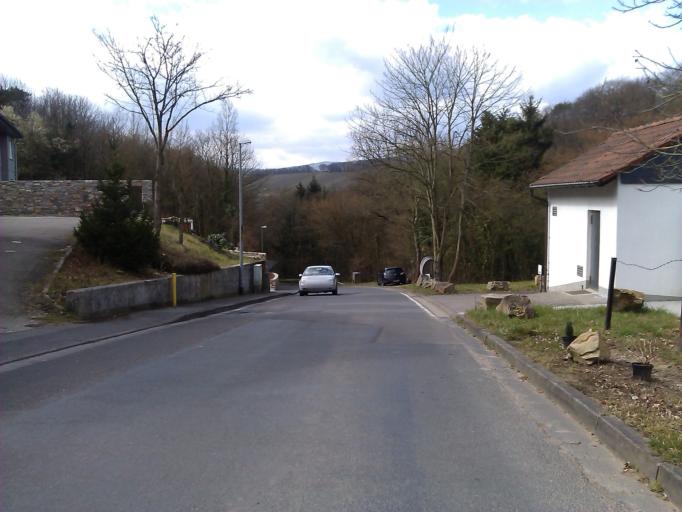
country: DE
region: Rheinland-Pfalz
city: Bingen am Rhein
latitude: 49.9931
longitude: 7.8862
